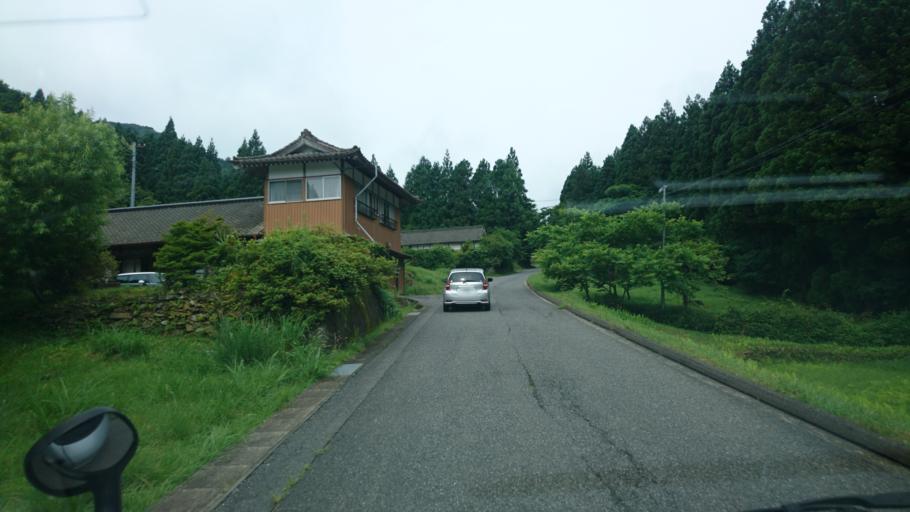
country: JP
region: Iwate
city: Ofunato
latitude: 39.1329
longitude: 141.7910
